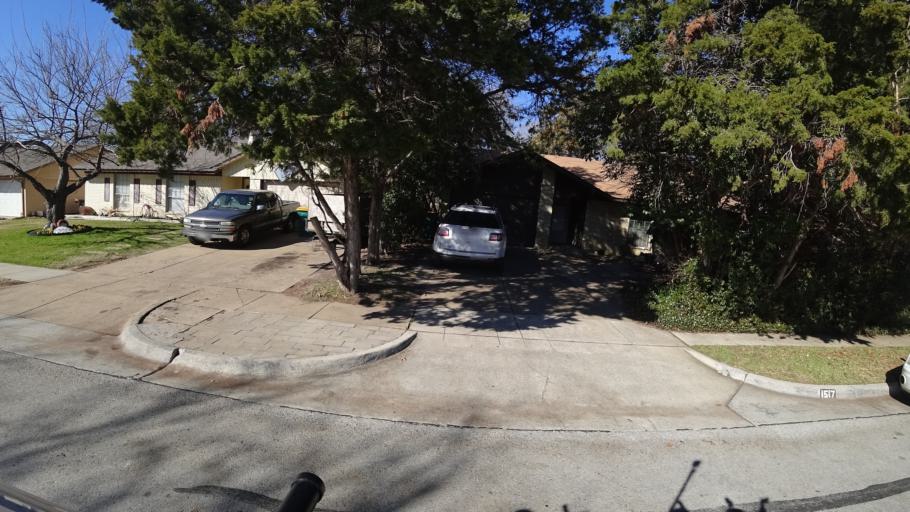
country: US
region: Texas
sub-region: Denton County
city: Lewisville
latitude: 33.0318
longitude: -97.0165
